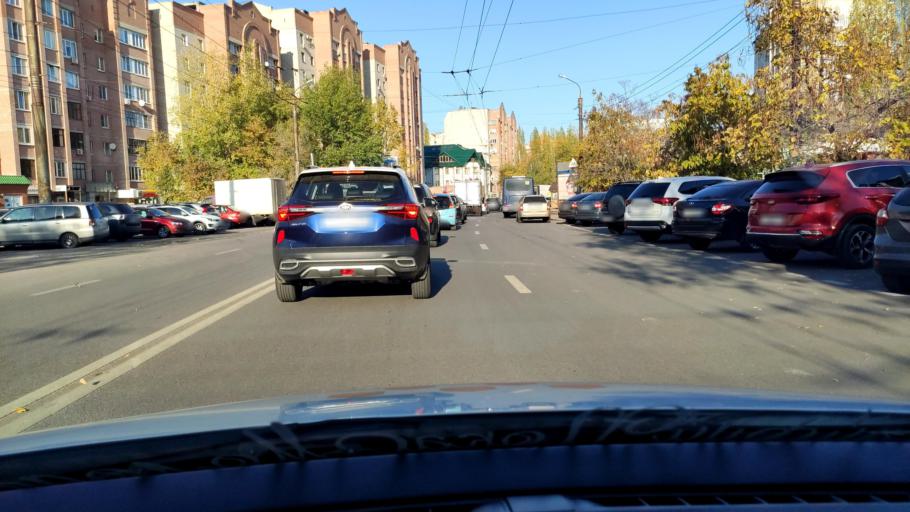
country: RU
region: Voronezj
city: Podgornoye
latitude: 51.7077
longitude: 39.1481
